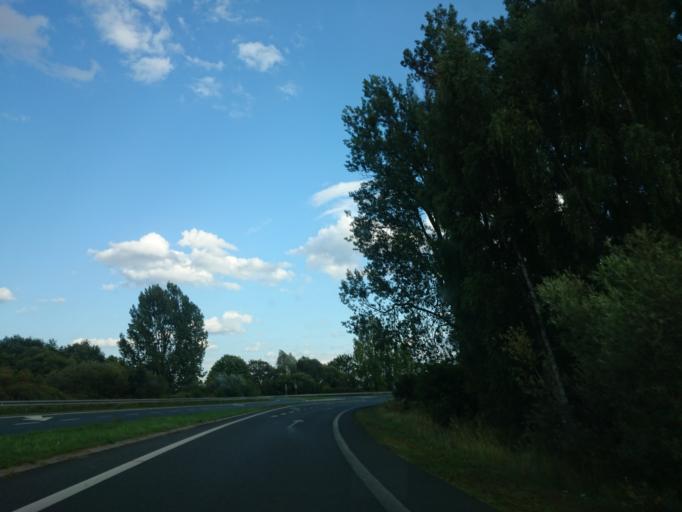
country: PL
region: West Pomeranian Voivodeship
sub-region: Powiat pyrzycki
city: Lipiany
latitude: 52.9901
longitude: 14.9777
